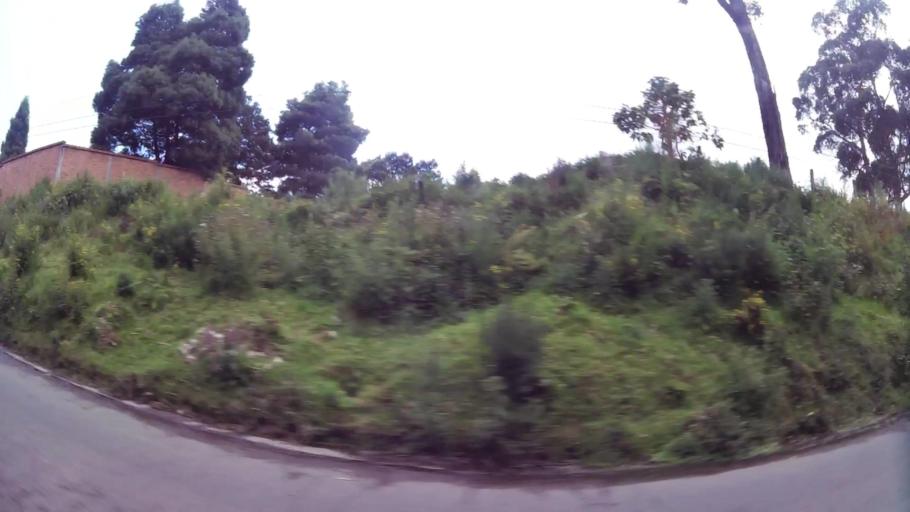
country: CO
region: Bogota D.C.
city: Bogota
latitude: 4.5912
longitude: -74.0642
